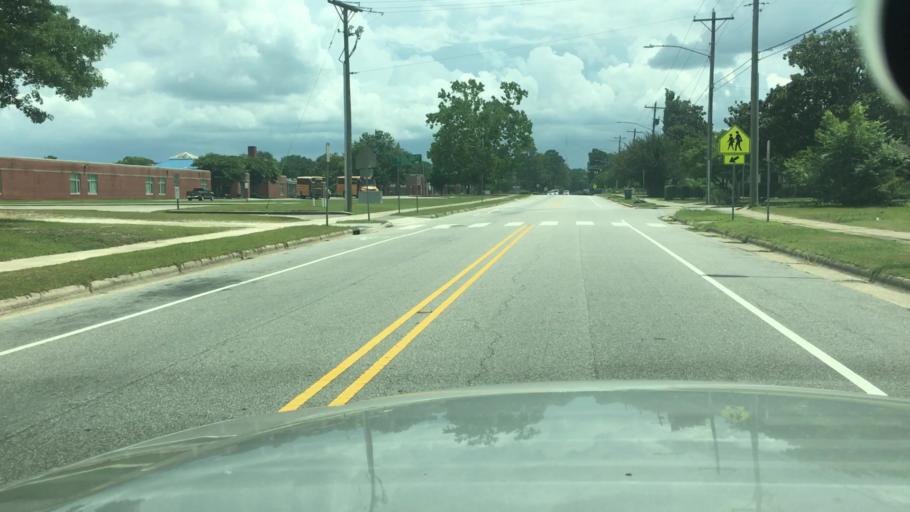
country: US
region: North Carolina
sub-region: Cumberland County
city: Fayetteville
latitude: 35.0860
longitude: -78.8982
